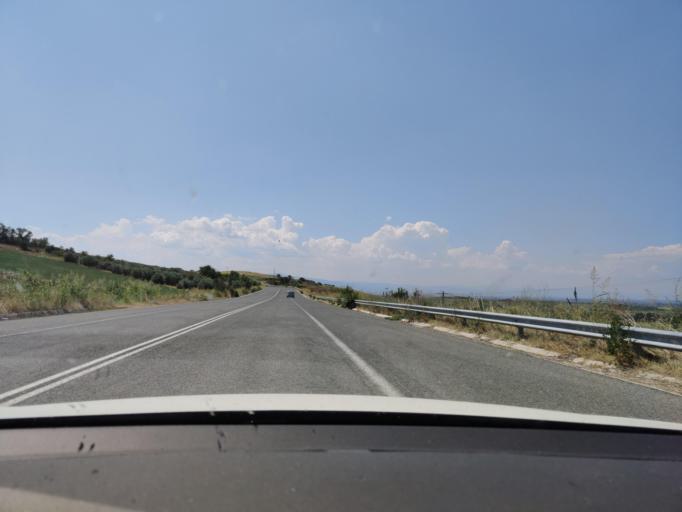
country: GR
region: Central Macedonia
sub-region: Nomos Serron
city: Draviskos
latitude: 40.9423
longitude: 23.8802
